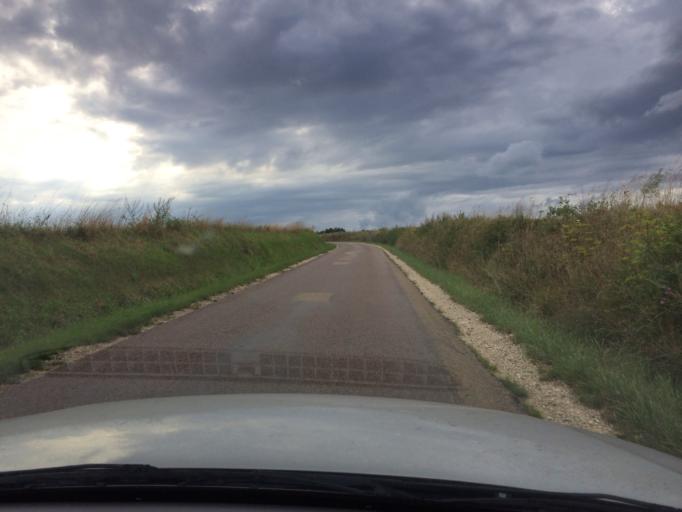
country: FR
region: Bourgogne
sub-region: Departement de l'Yonne
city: Fleury-la-Vallee
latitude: 47.8692
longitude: 3.4297
